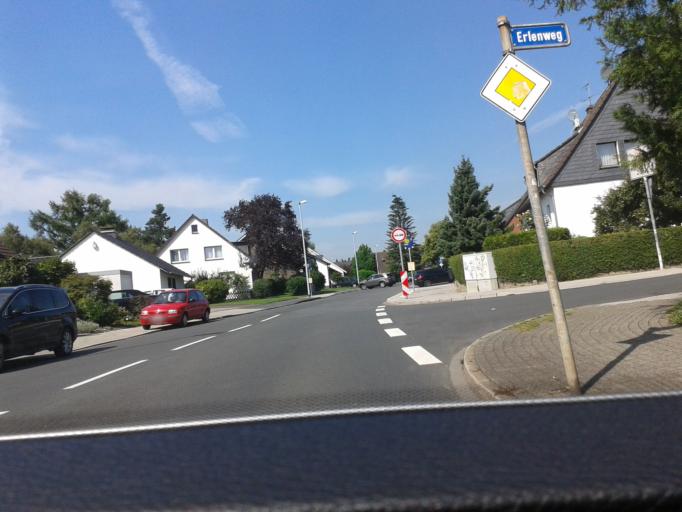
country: DE
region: North Rhine-Westphalia
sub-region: Regierungsbezirk Dusseldorf
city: Muelheim (Ruhr)
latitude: 51.3927
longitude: 6.8586
